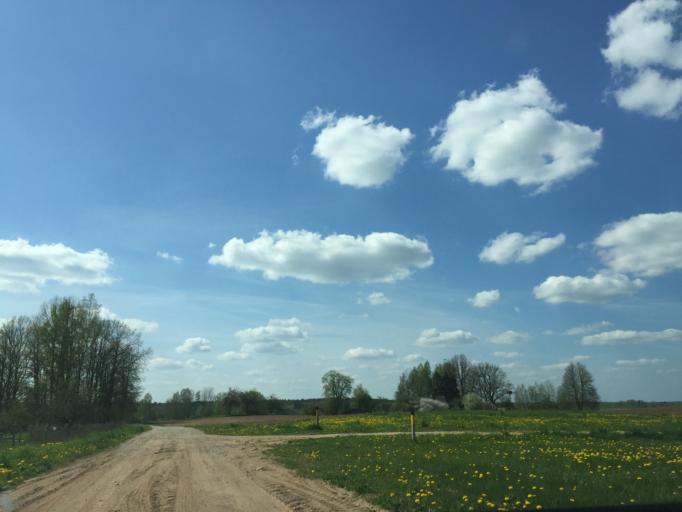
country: LV
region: Vecumnieki
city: Vecumnieki
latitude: 56.4822
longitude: 24.5534
